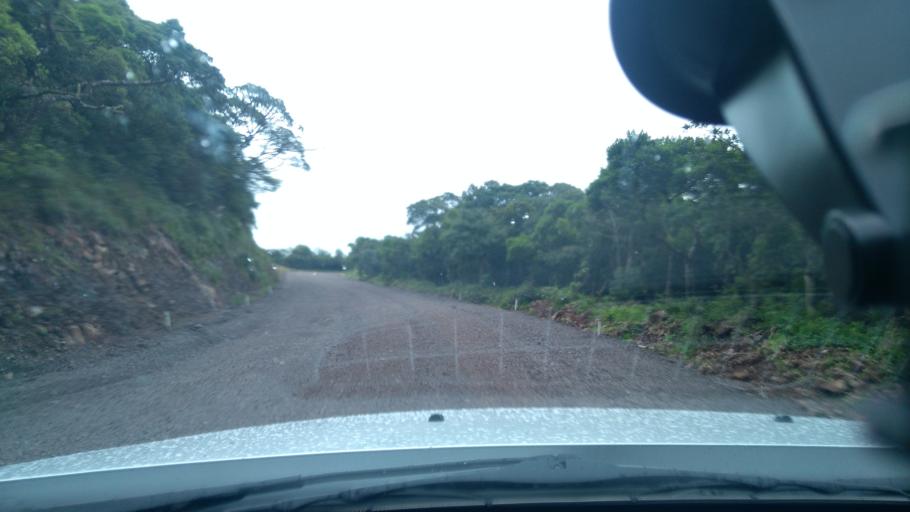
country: BR
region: Rio Grande do Sul
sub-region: Torres
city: Torres
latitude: -29.1796
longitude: -50.0227
